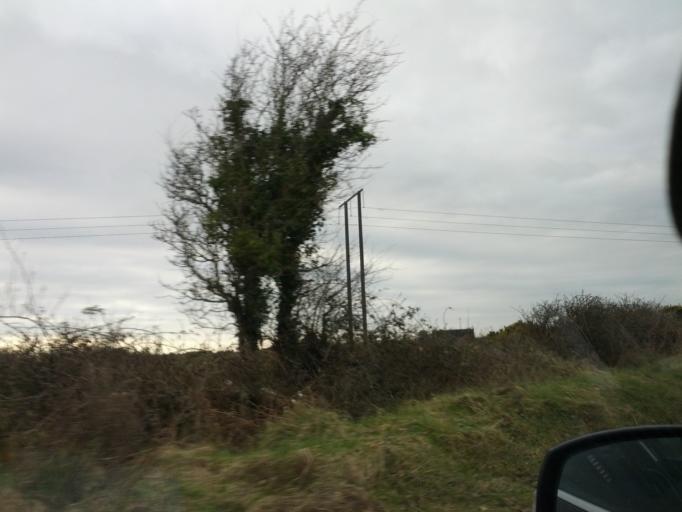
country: IE
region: Connaught
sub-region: County Galway
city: Gort
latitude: 53.1593
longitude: -8.8525
